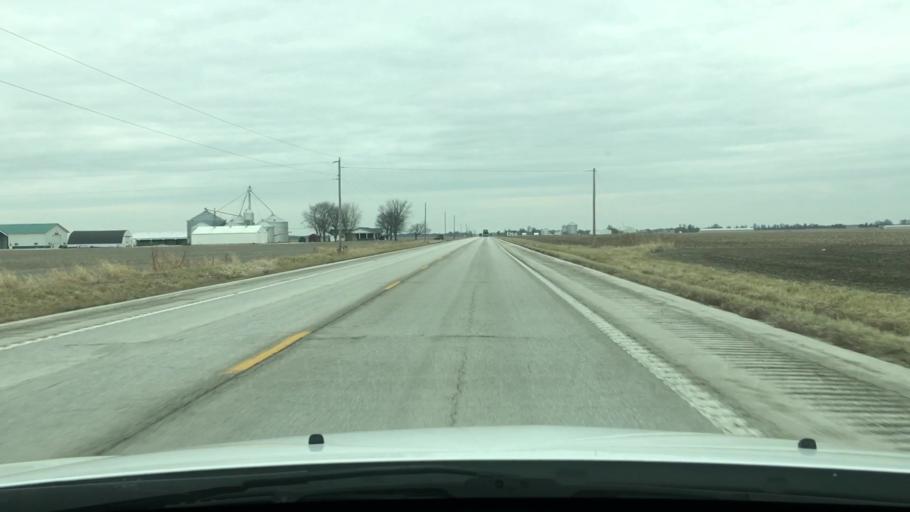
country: US
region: Missouri
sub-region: Audrain County
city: Vandalia
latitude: 39.2676
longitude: -91.6447
